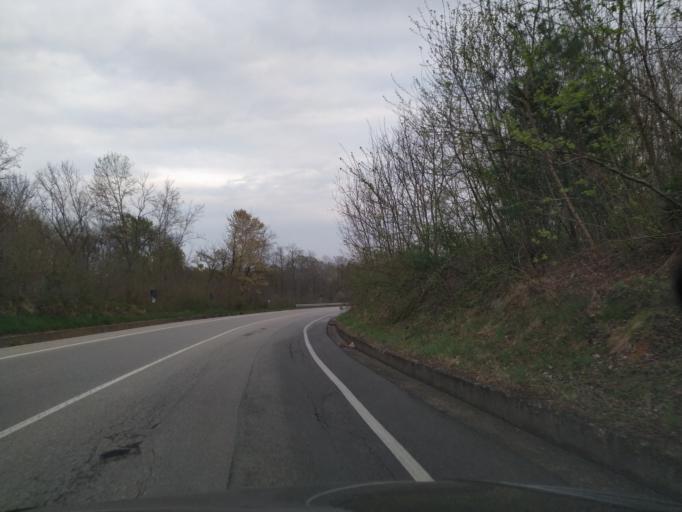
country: IT
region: Piedmont
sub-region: Provincia di Novara
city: Cavallirio
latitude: 45.6543
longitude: 8.4073
